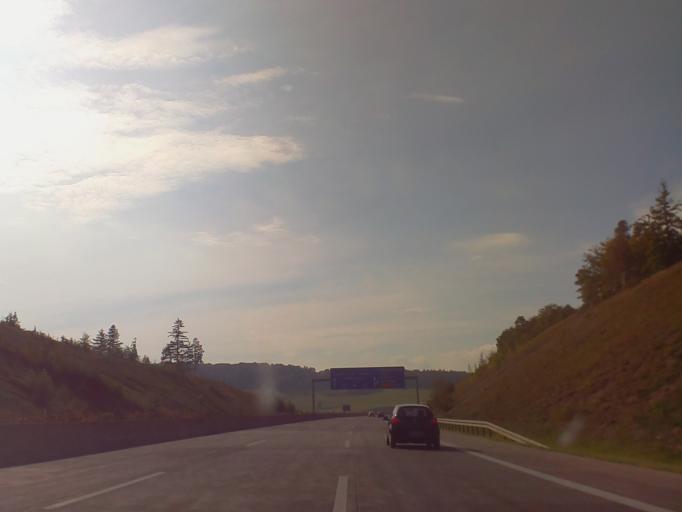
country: DE
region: Thuringia
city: Krauthausen
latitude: 51.0082
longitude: 10.2816
